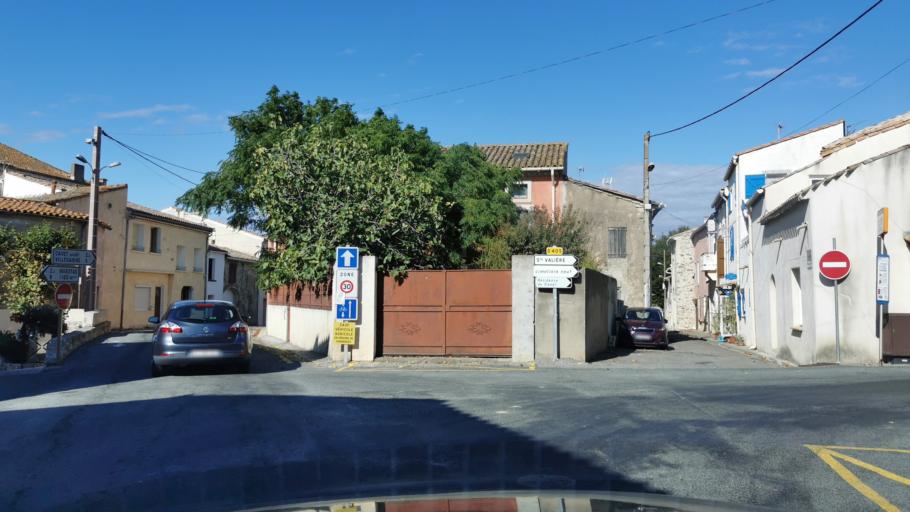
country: FR
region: Languedoc-Roussillon
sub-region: Departement de l'Aude
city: Ginestas
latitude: 43.2488
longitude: 2.8595
